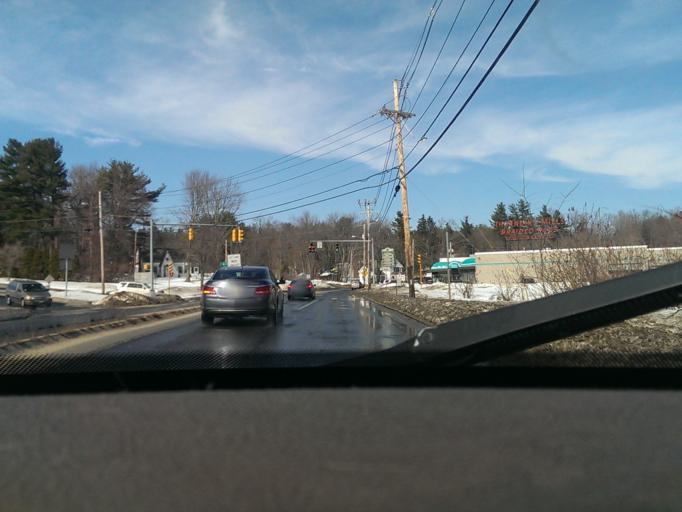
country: US
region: Massachusetts
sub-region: Hampden County
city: Palmer
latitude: 42.1781
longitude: -72.3193
